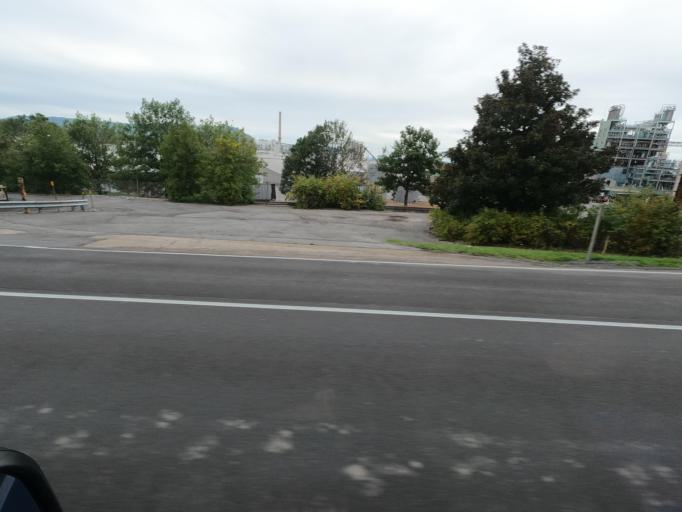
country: US
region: Tennessee
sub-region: Sullivan County
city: Colonial Heights
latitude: 36.5125
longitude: -82.5348
